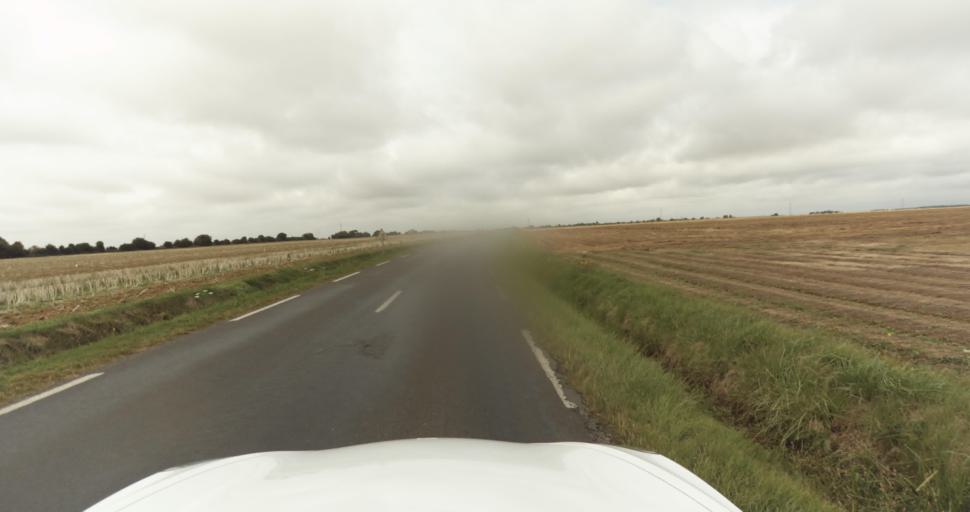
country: FR
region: Haute-Normandie
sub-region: Departement de l'Eure
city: Claville
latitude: 49.0770
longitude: 1.0605
